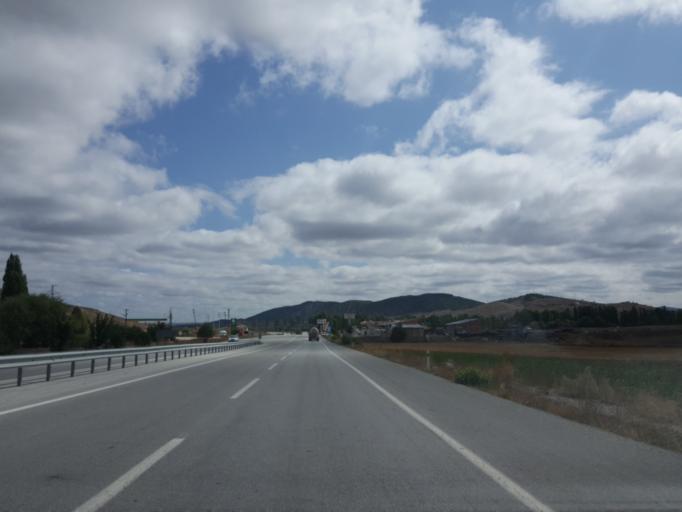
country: TR
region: Sivas
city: Yavu
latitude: 39.7961
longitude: 36.1924
